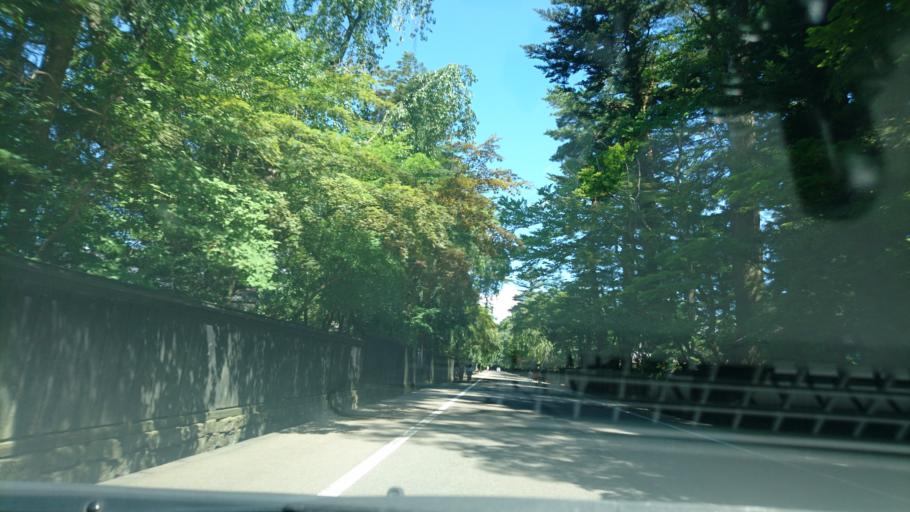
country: JP
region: Akita
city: Kakunodatemachi
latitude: 39.5975
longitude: 140.5622
